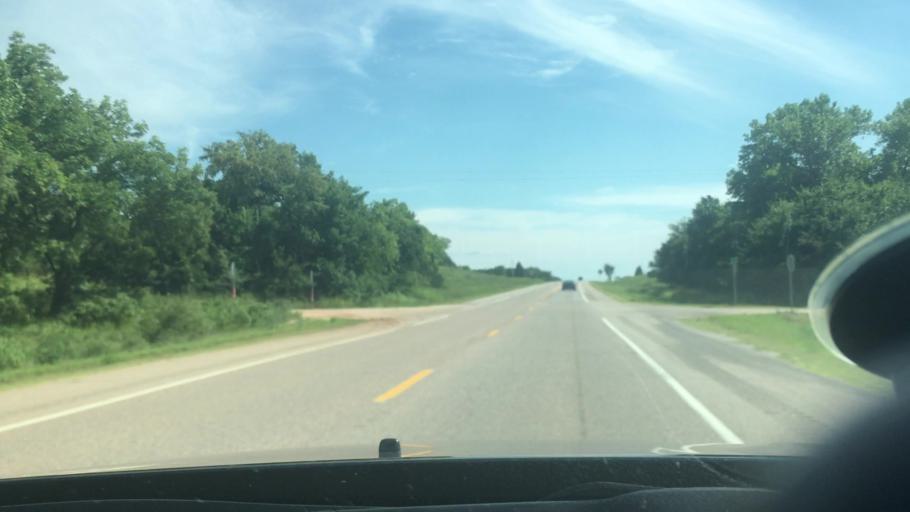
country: US
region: Oklahoma
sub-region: Seminole County
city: Maud
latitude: 35.0730
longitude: -96.6788
